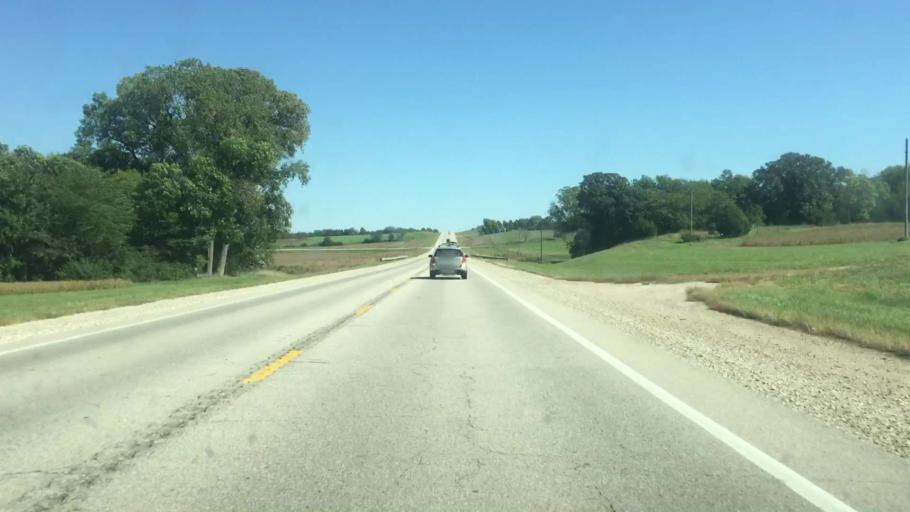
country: US
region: Kansas
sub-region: Nemaha County
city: Seneca
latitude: 39.8421
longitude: -96.0041
